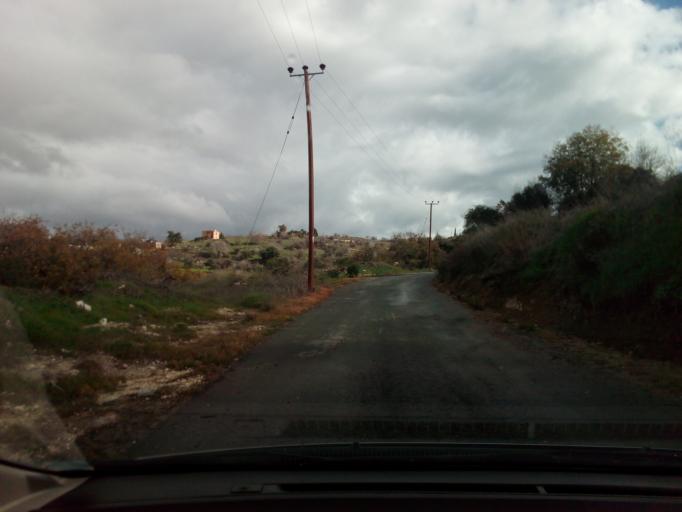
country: CY
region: Pafos
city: Tala
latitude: 34.9205
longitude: 32.5105
